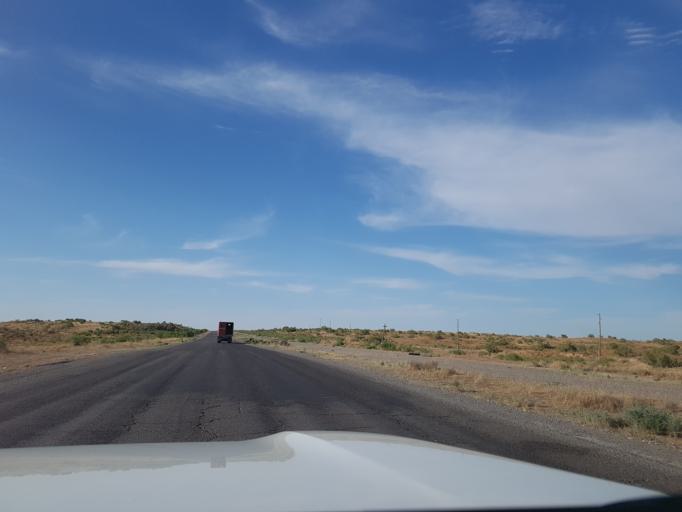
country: TM
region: Mary
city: Bayramaly
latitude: 37.9011
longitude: 62.6185
